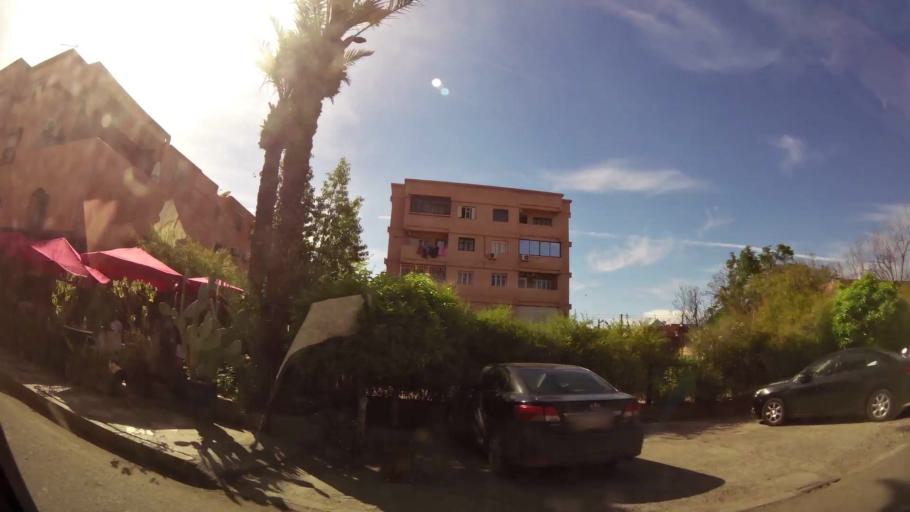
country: MA
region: Marrakech-Tensift-Al Haouz
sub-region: Marrakech
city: Marrakesh
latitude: 31.6505
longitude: -8.0118
